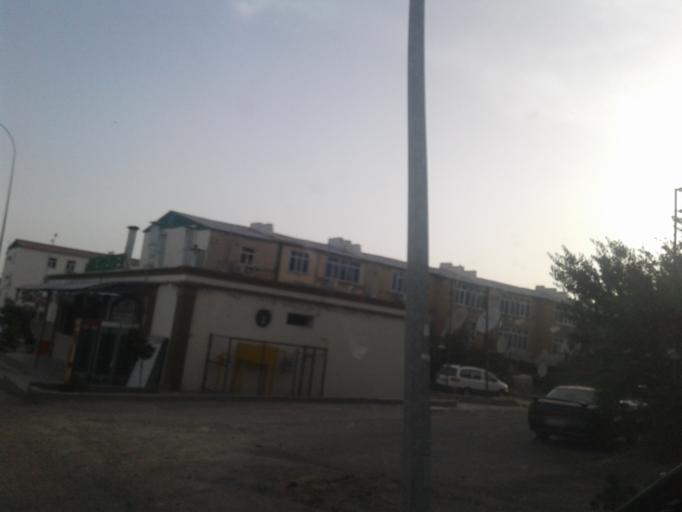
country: TM
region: Balkan
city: Turkmenbasy
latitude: 40.0020
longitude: 52.9653
